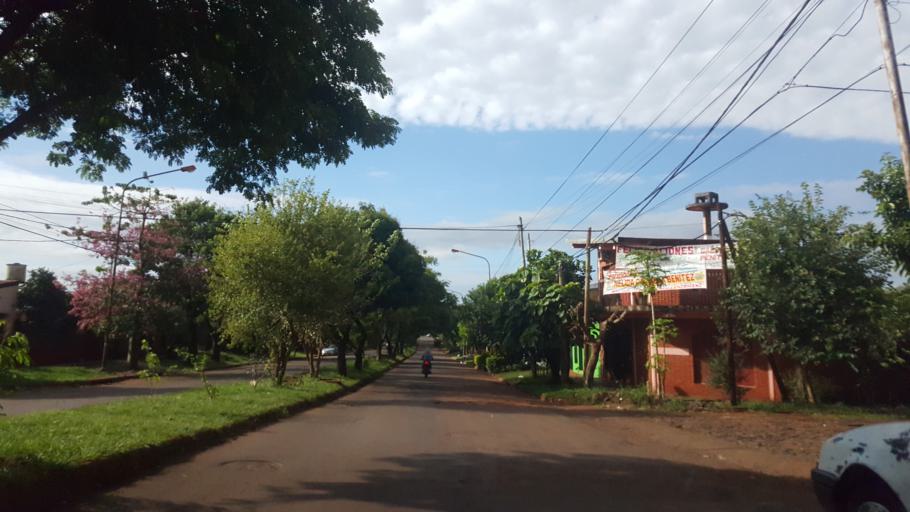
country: AR
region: Misiones
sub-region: Departamento de Capital
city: Posadas
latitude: -27.3834
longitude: -55.9339
